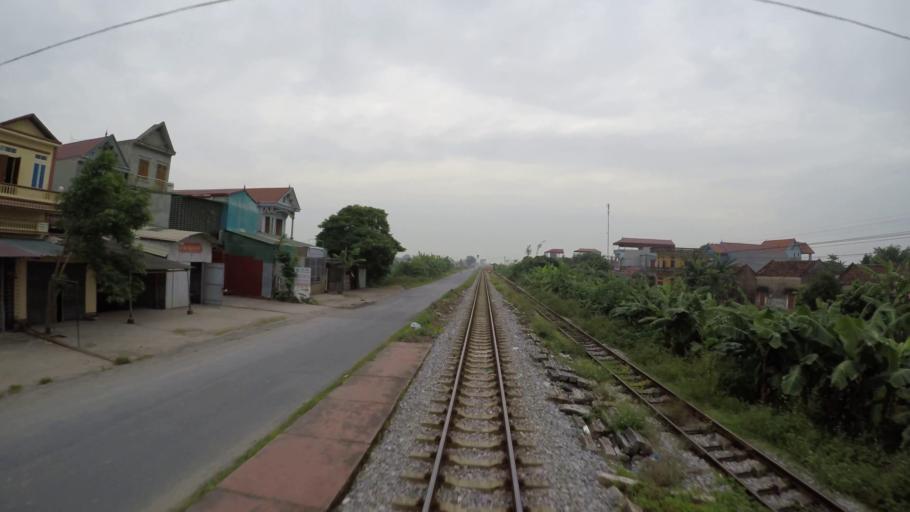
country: VN
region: Hung Yen
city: Ban Yen Nhan
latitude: 20.9726
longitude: 106.0964
